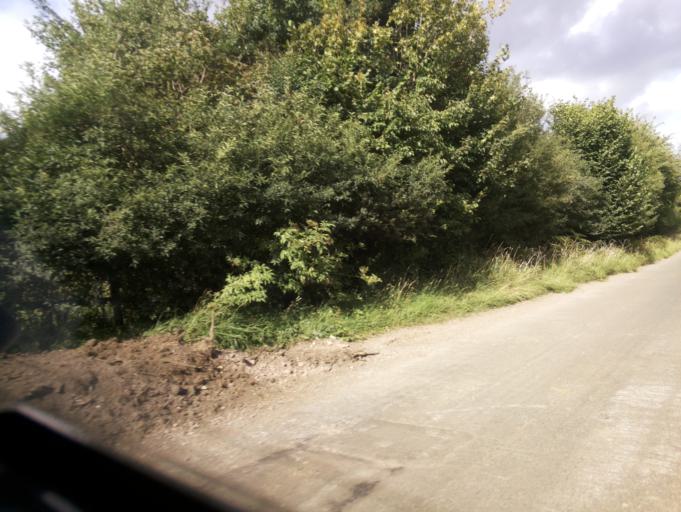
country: GB
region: England
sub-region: Gloucestershire
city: Coates
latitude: 51.7391
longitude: -2.0445
